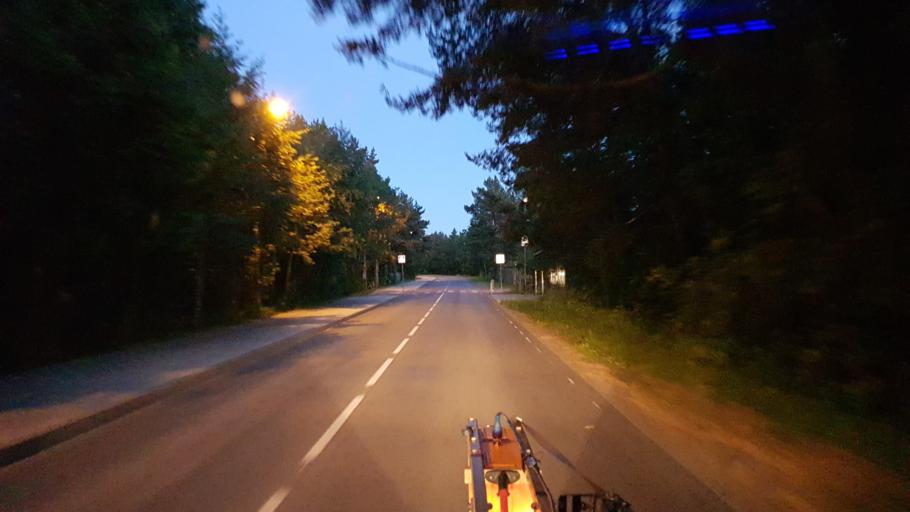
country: EE
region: Harju
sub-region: Harku vald
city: Tabasalu
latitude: 59.4474
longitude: 24.5910
